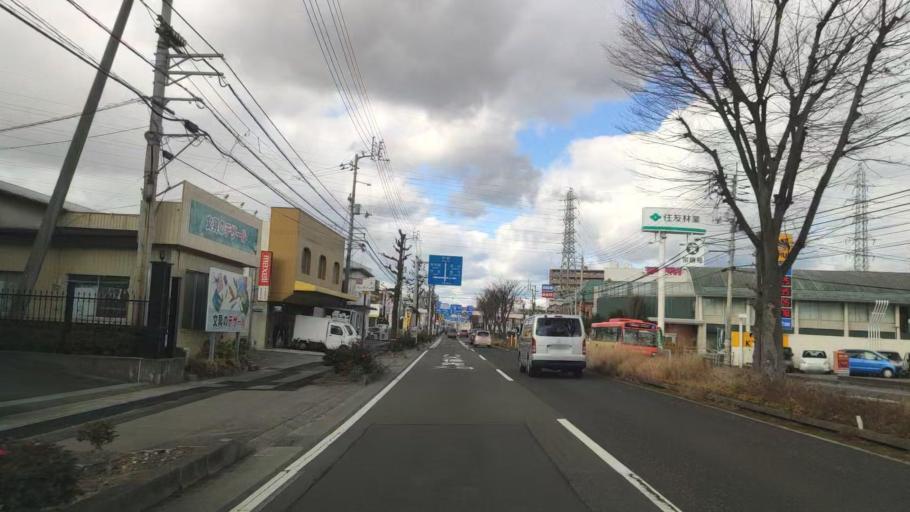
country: JP
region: Ehime
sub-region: Shikoku-chuo Shi
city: Matsuyama
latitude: 33.8192
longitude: 132.7768
